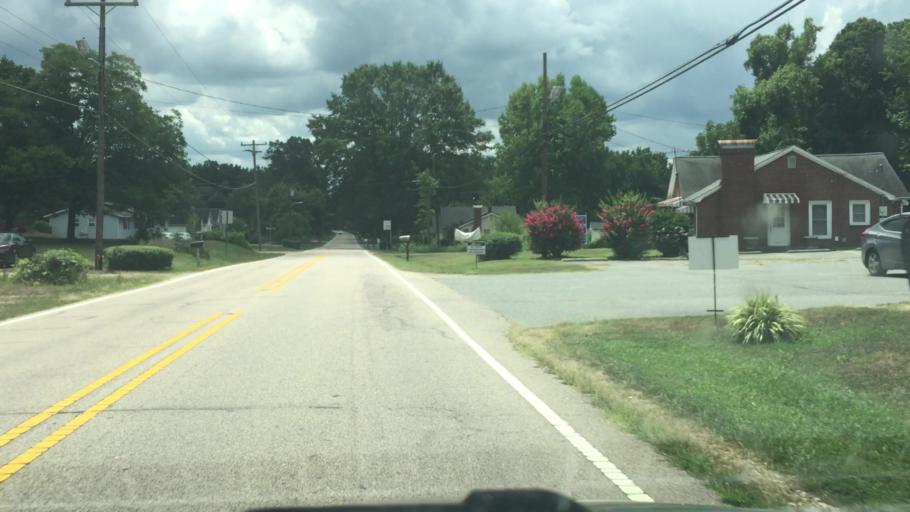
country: US
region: North Carolina
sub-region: Rowan County
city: Enochville
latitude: 35.4949
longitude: -80.6656
